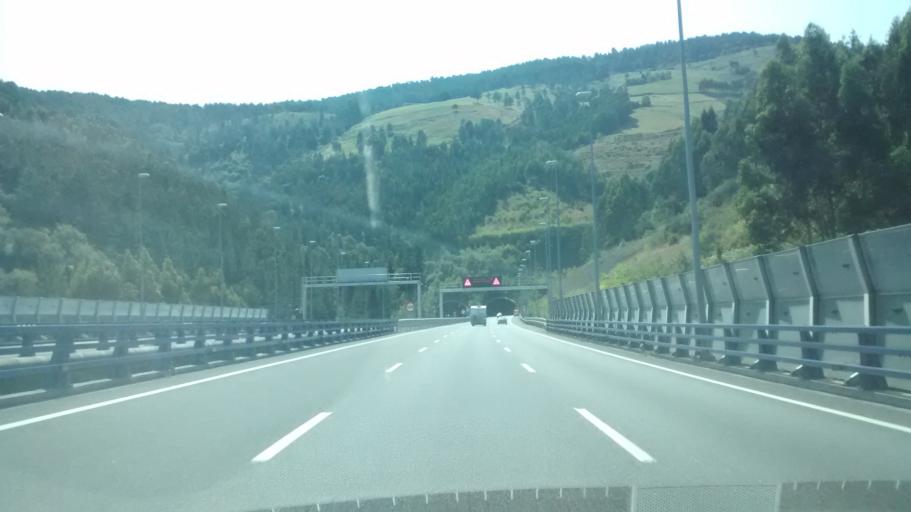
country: ES
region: Basque Country
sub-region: Bizkaia
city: Alonsotegi
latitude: 43.2692
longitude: -2.9971
